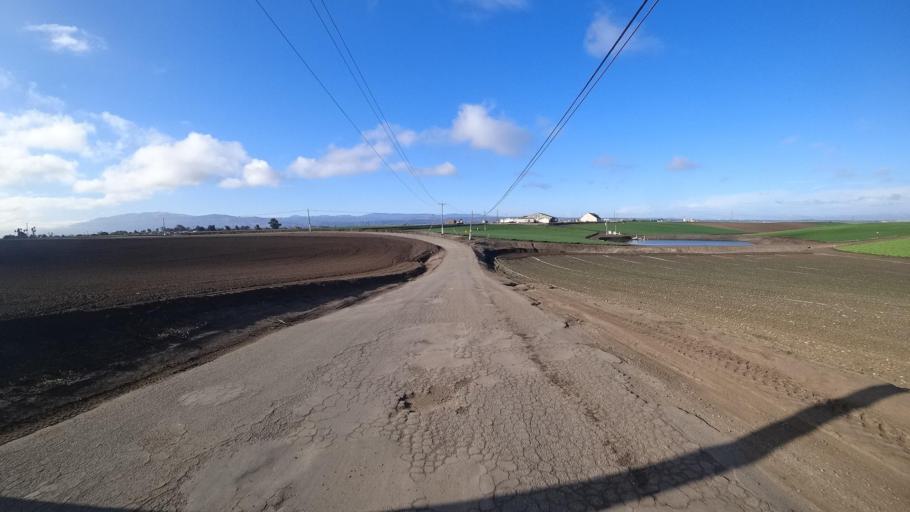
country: US
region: California
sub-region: Monterey County
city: Boronda
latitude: 36.7080
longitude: -121.6785
